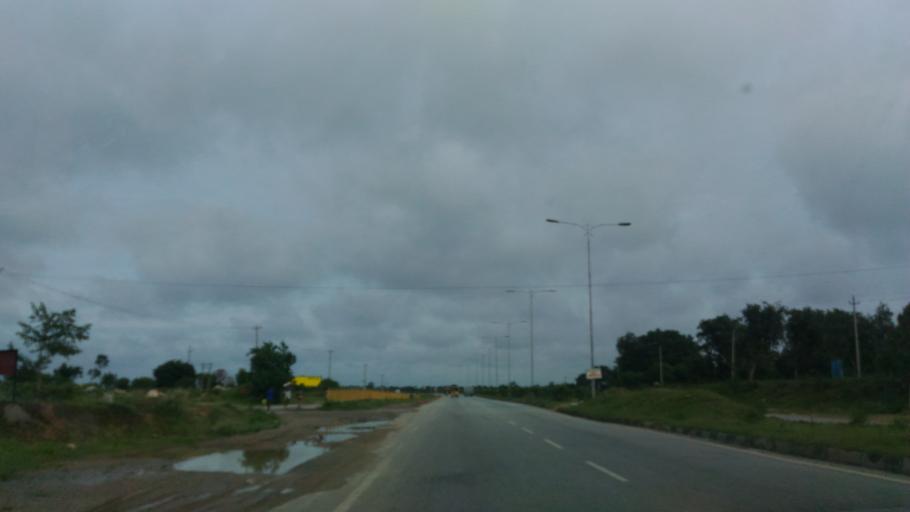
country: IN
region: Karnataka
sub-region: Tumkur
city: Kunigal
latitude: 13.0022
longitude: 76.9590
